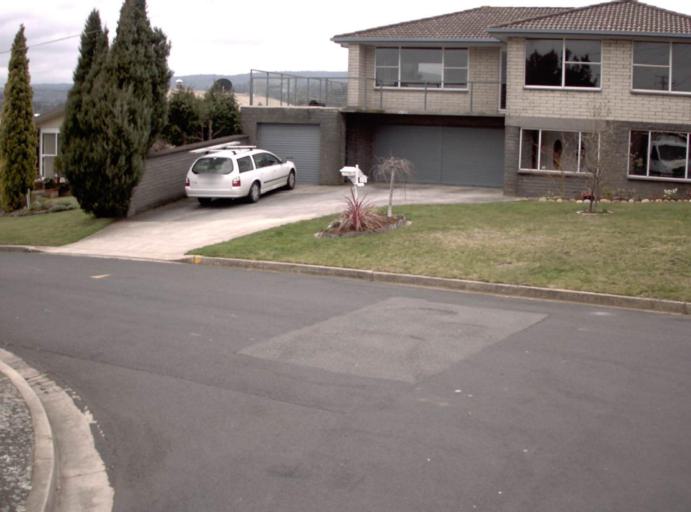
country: AU
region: Tasmania
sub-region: Launceston
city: Newstead
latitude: -41.4476
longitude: 147.1788
